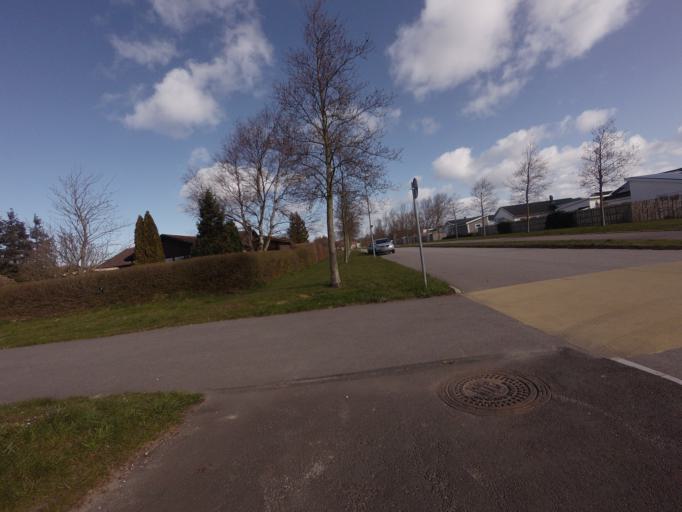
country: SE
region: Skane
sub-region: Hoganas Kommun
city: Hoganas
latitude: 56.1734
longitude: 12.5730
